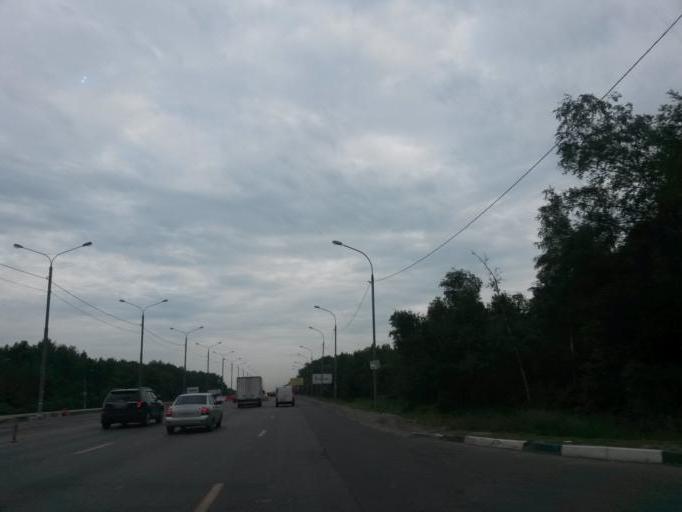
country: RU
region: Moskovskaya
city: Shcherbinka
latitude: 55.5009
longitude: 37.6096
